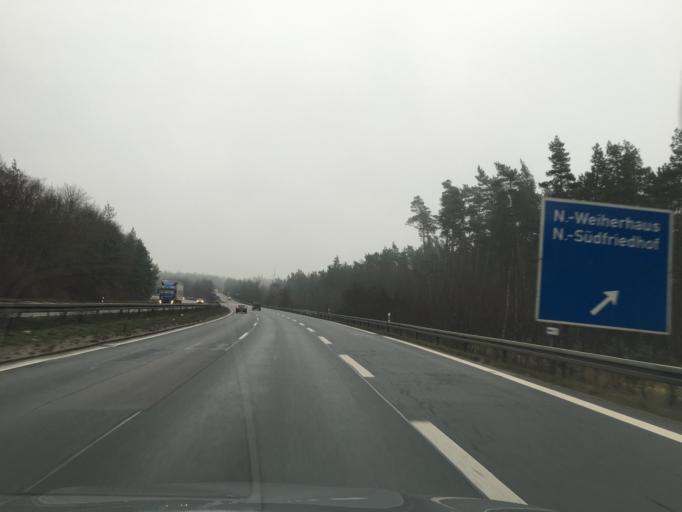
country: DE
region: Bavaria
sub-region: Regierungsbezirk Mittelfranken
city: Nuernberg
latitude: 49.3970
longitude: 11.0780
